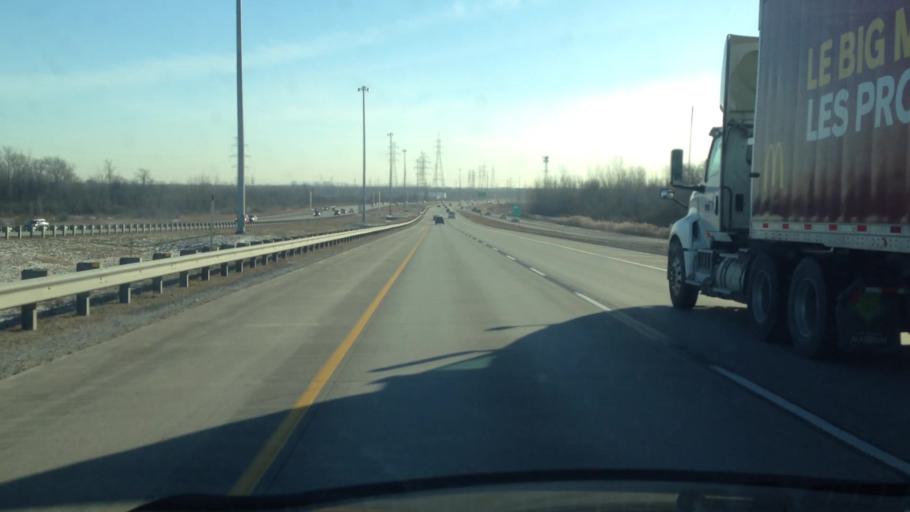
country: CA
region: Quebec
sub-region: Laurentides
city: Boisbriand
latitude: 45.5981
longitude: -73.8610
